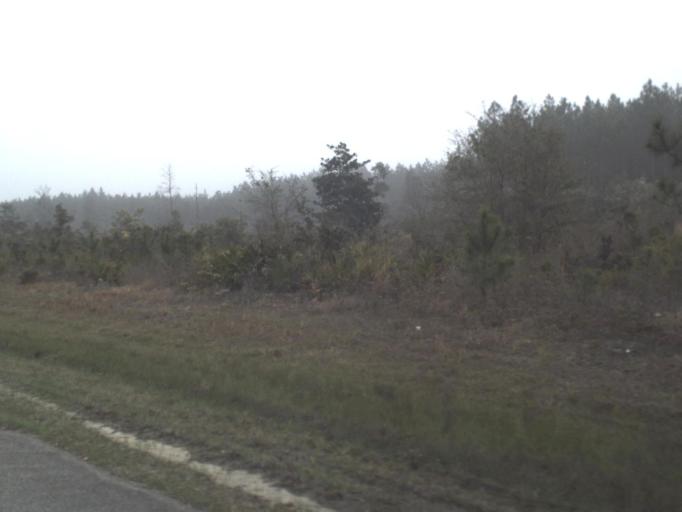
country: US
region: Florida
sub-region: Gadsden County
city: Gretna
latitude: 30.4977
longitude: -84.7178
